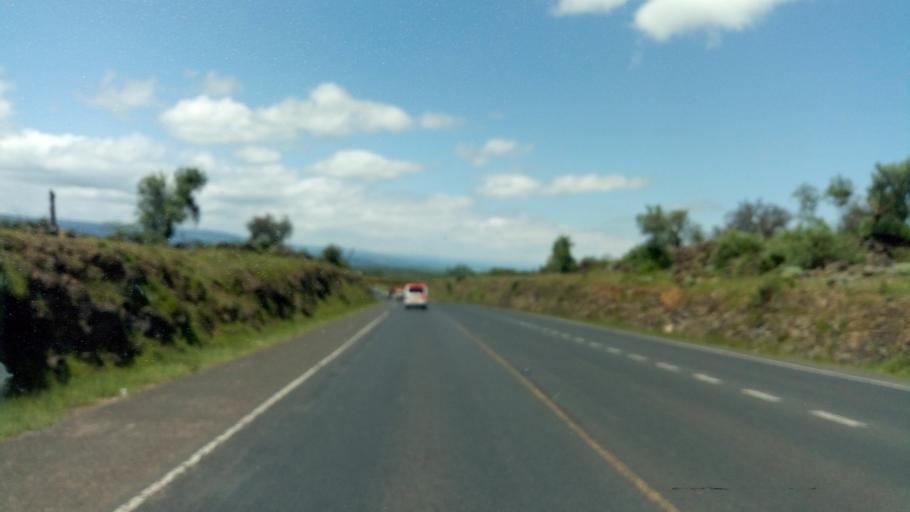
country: KE
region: Nakuru
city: Naivasha
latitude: -0.5417
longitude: 36.3385
